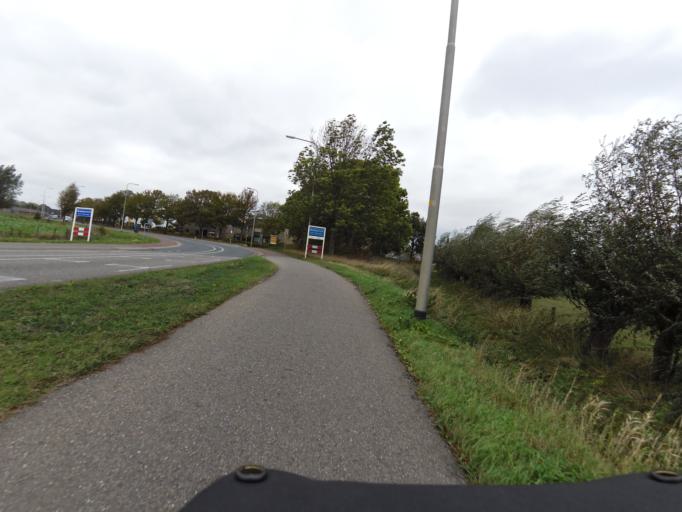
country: NL
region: Gelderland
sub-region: Gemeente Zevenaar
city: Zevenaar
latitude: 51.9031
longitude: 6.1108
